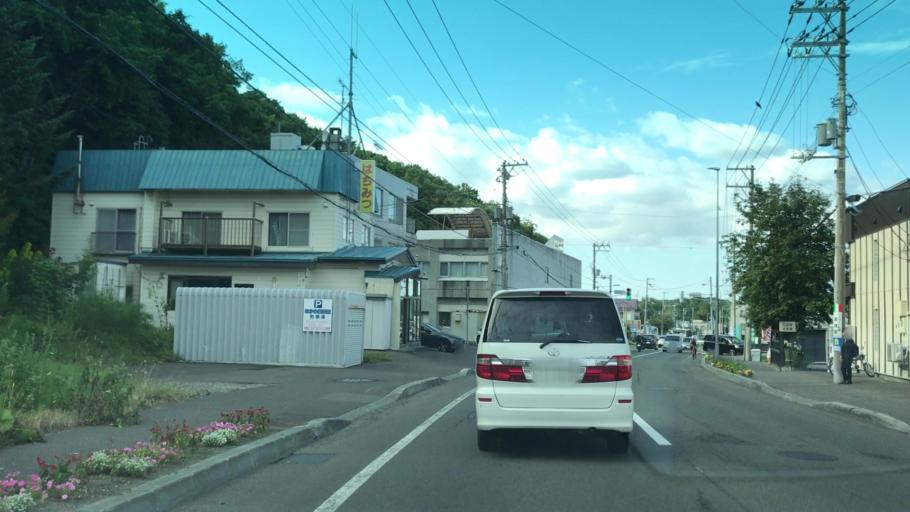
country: JP
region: Hokkaido
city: Sapporo
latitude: 42.9660
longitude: 141.3427
